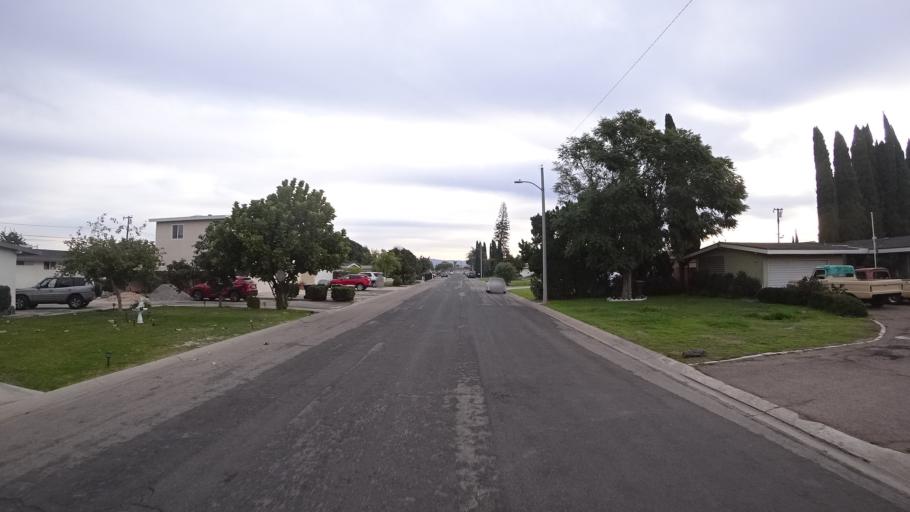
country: US
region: California
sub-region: Orange County
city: Garden Grove
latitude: 33.7702
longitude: -117.9270
